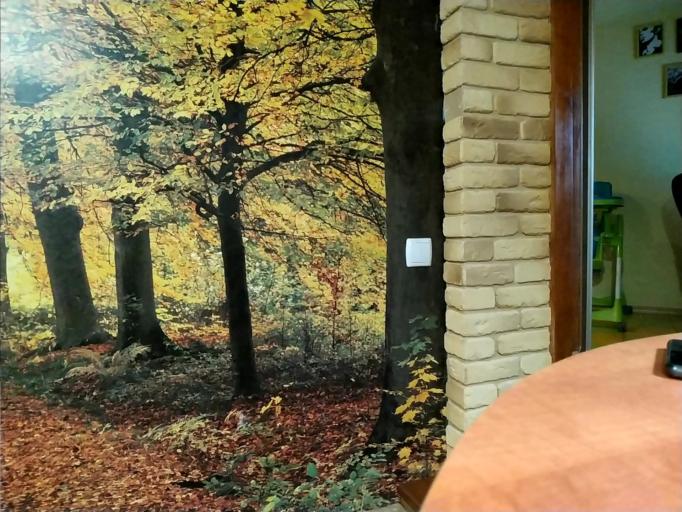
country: BY
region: Minsk
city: Il'ya
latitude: 54.4238
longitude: 27.5113
